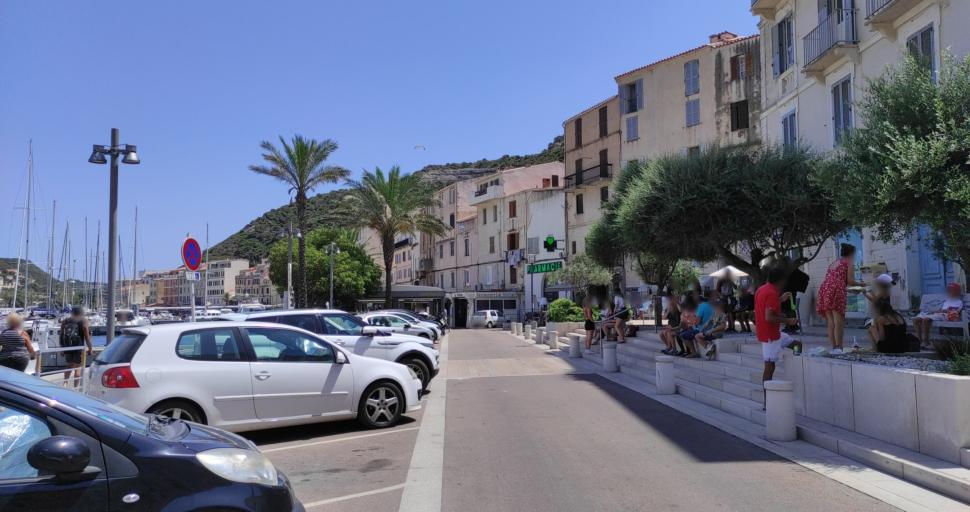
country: FR
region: Corsica
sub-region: Departement de la Corse-du-Sud
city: Bonifacio
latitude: 41.3884
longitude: 9.1615
